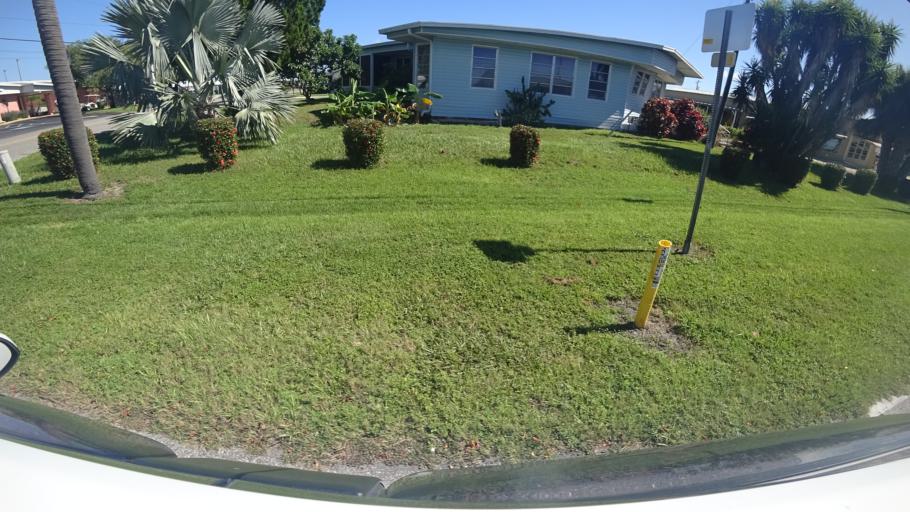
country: US
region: Florida
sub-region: Manatee County
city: Bayshore Gardens
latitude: 27.4184
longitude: -82.5805
